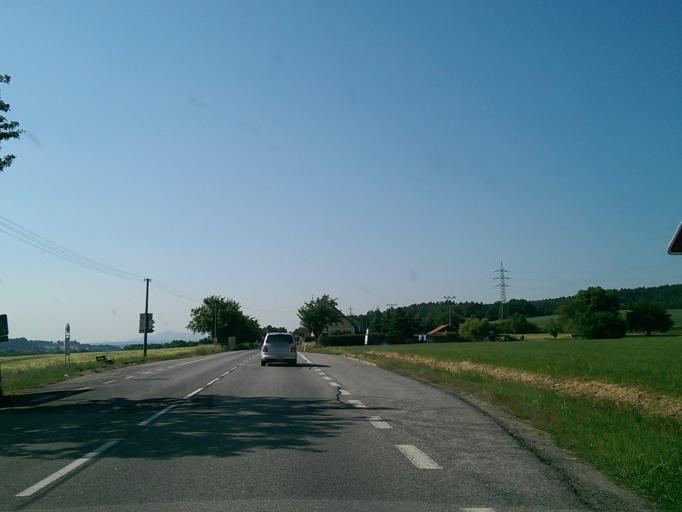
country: CZ
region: Liberecky
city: Rovensko pod Troskami
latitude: 50.5255
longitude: 15.2441
